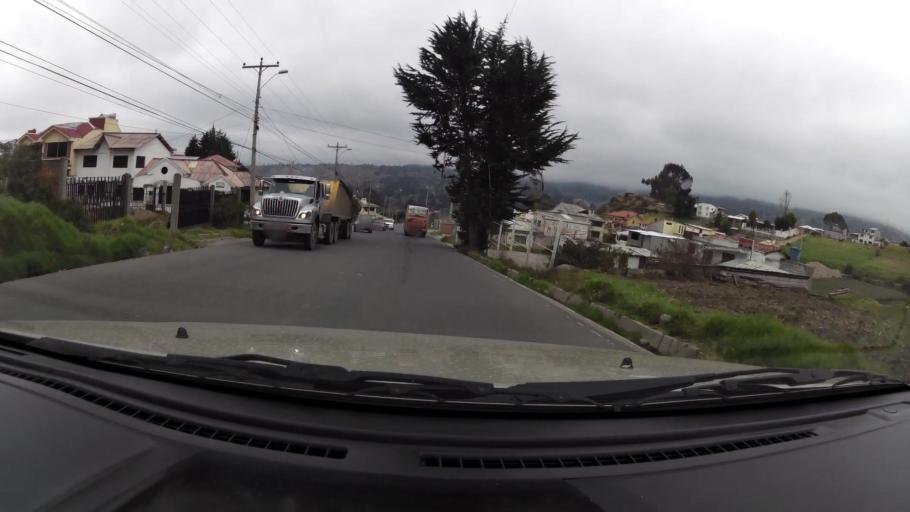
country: EC
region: Canar
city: Canar
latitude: -2.5360
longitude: -78.9320
